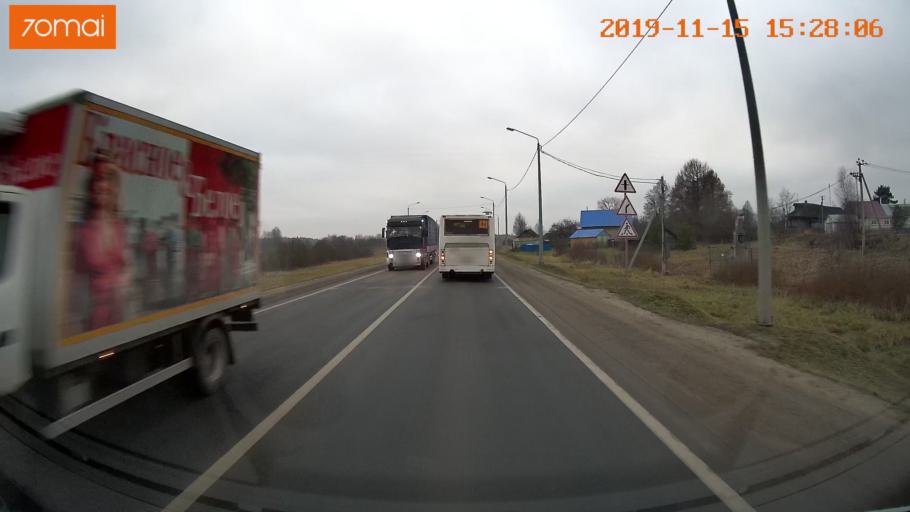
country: RU
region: Jaroslavl
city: Danilov
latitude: 58.1350
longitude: 40.1377
